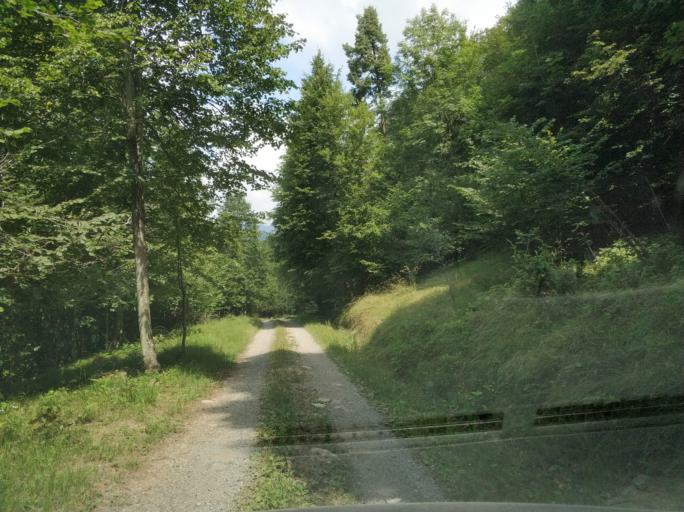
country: IT
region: Piedmont
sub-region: Provincia di Torino
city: Viu
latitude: 45.2026
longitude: 7.3932
